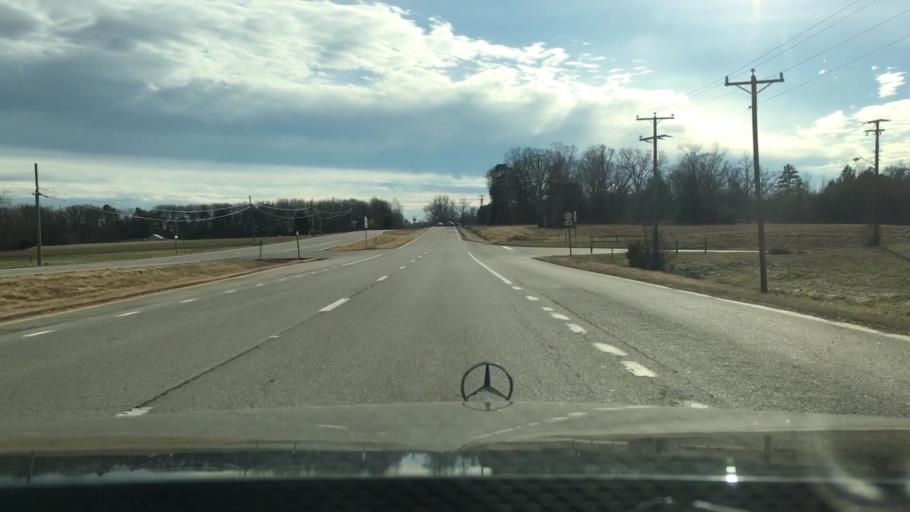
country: US
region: Virginia
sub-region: Pittsylvania County
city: Mount Hermon
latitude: 36.7306
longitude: -79.3829
